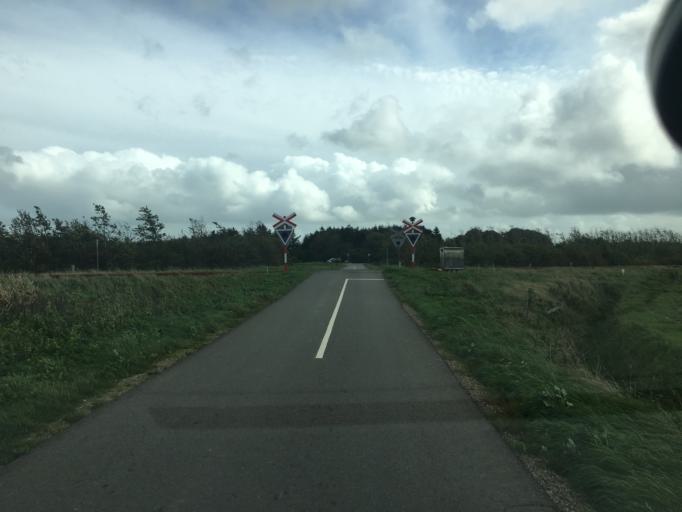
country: DK
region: South Denmark
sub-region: Tonder Kommune
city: Sherrebek
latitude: 55.0766
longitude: 8.8236
